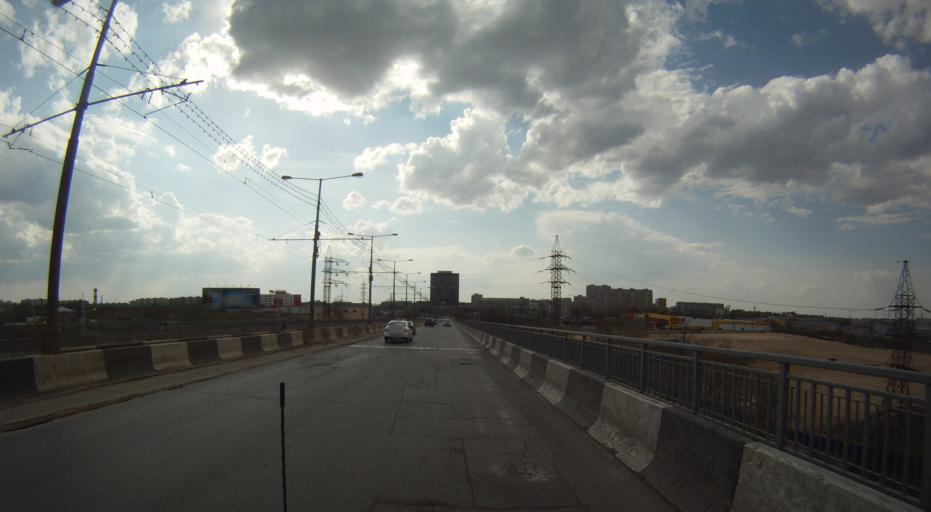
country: RU
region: Nizjnij Novgorod
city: Nizhniy Novgorod
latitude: 56.2989
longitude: 43.9545
